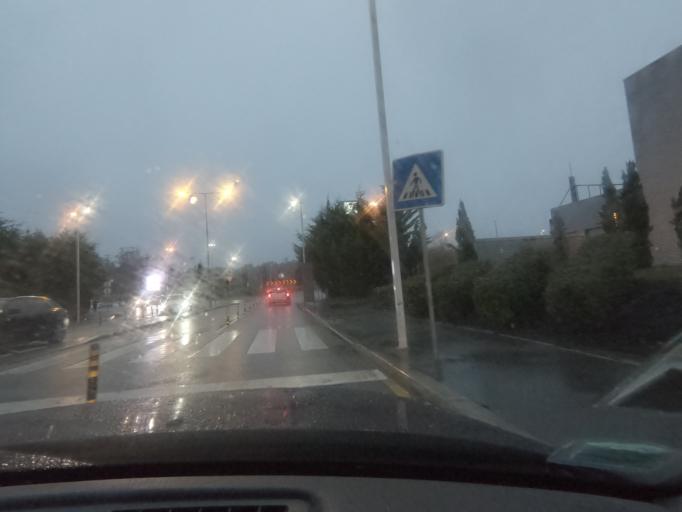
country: PT
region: Porto
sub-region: Vila do Conde
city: Arvore
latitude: 41.3010
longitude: -8.7080
